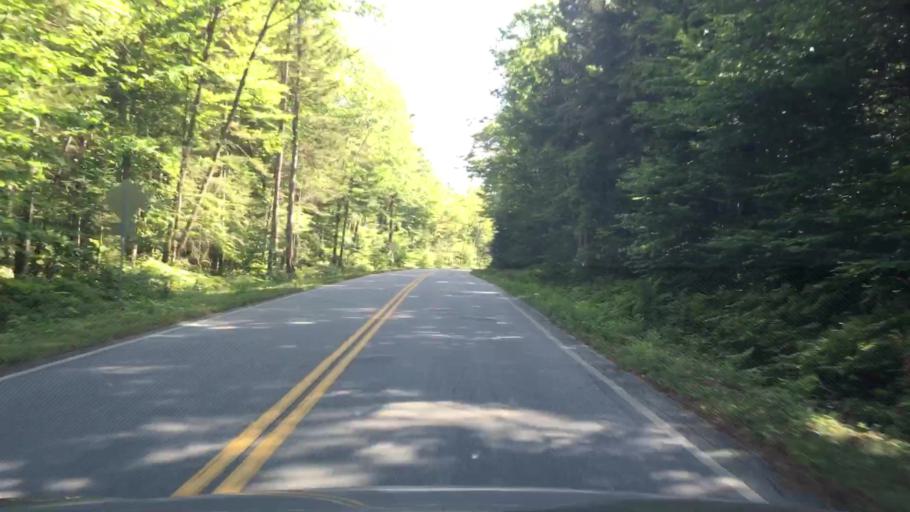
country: US
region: New Hampshire
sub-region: Carroll County
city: North Conway
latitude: 44.0684
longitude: -71.2827
